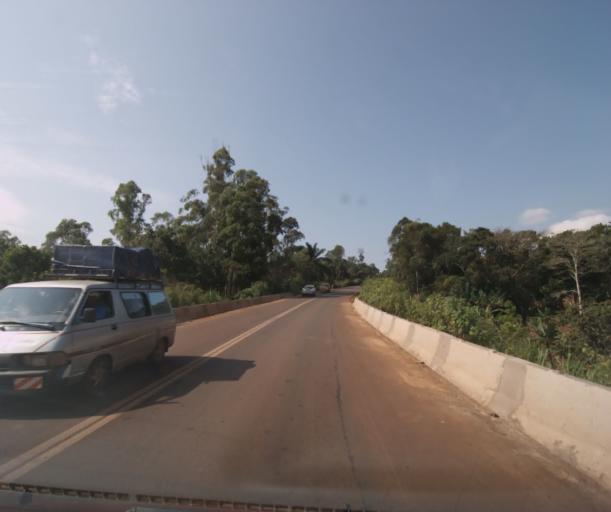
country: CM
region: West
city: Mbouda
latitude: 5.6027
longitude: 10.2944
